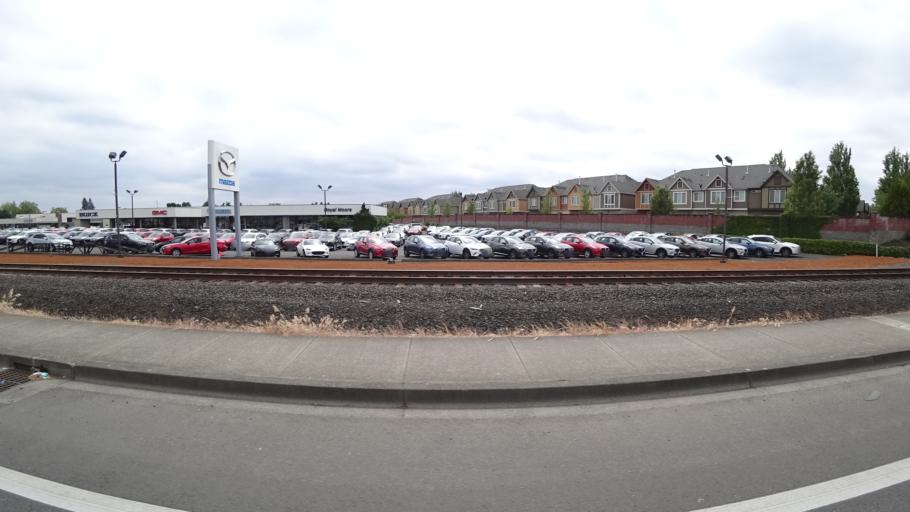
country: US
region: Oregon
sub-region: Washington County
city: Hillsboro
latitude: 45.5103
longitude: -122.9698
